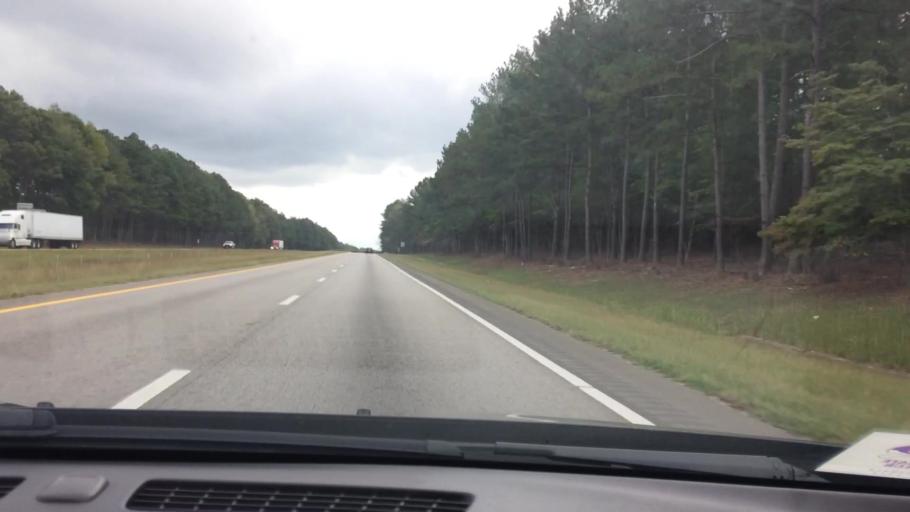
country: US
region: North Carolina
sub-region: Wake County
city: Zebulon
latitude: 35.8161
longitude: -78.2491
